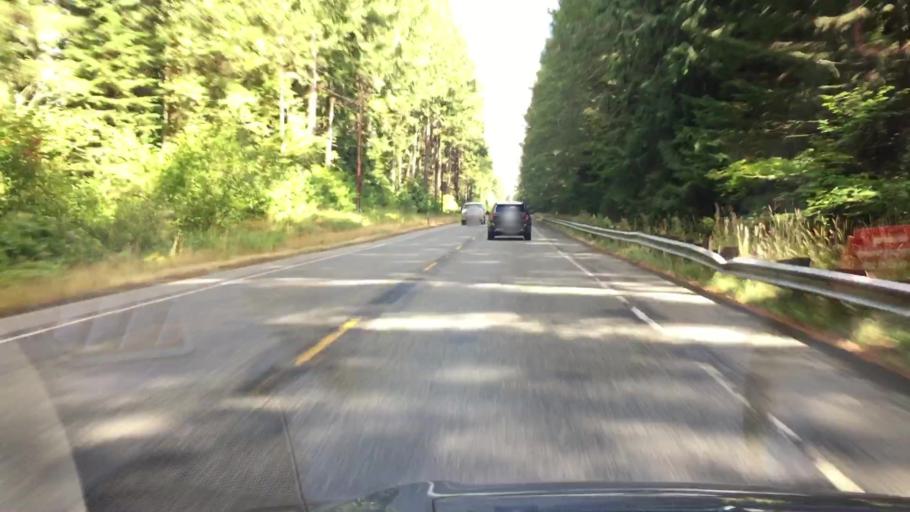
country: US
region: Washington
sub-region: Pierce County
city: Eatonville
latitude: 46.7563
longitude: -122.0801
